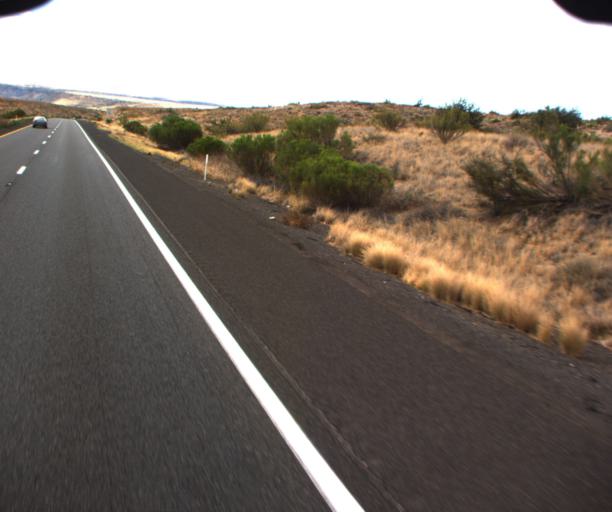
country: US
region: Arizona
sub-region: Yavapai County
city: Cordes Lakes
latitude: 34.2586
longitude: -112.1165
